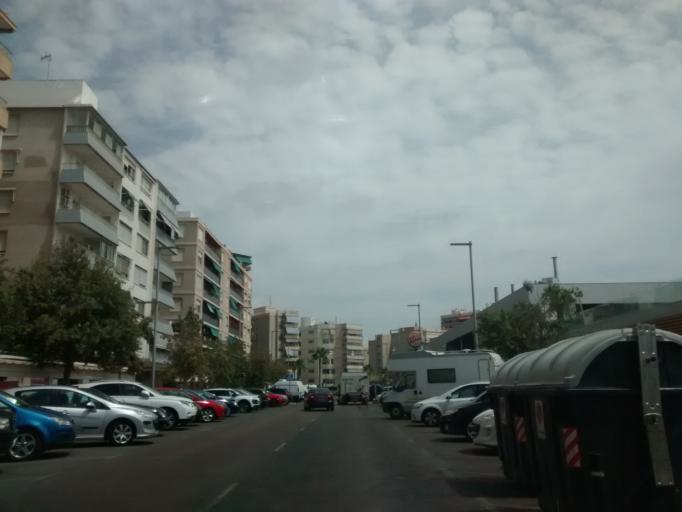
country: ES
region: Valencia
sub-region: Provincia de Alicante
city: Santa Pola
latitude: 38.1914
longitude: -0.5618
